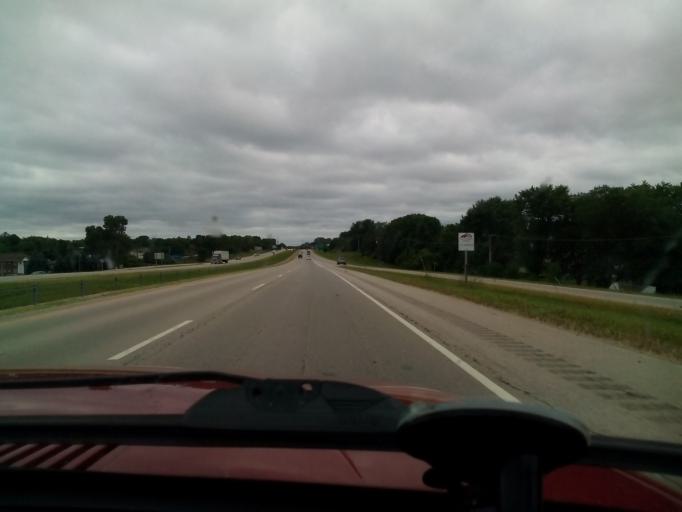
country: US
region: Wisconsin
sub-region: Dane County
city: Sun Prairie
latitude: 43.1969
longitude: -89.2119
